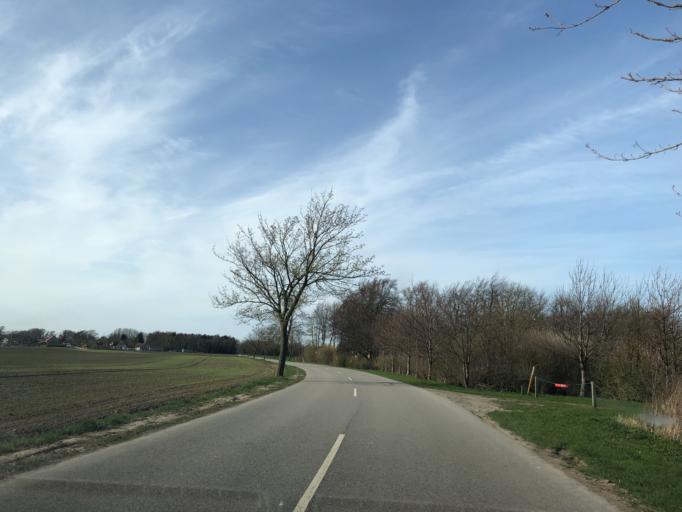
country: DK
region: Zealand
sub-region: Stevns Kommune
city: Store Heddinge
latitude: 55.2927
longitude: 12.4459
